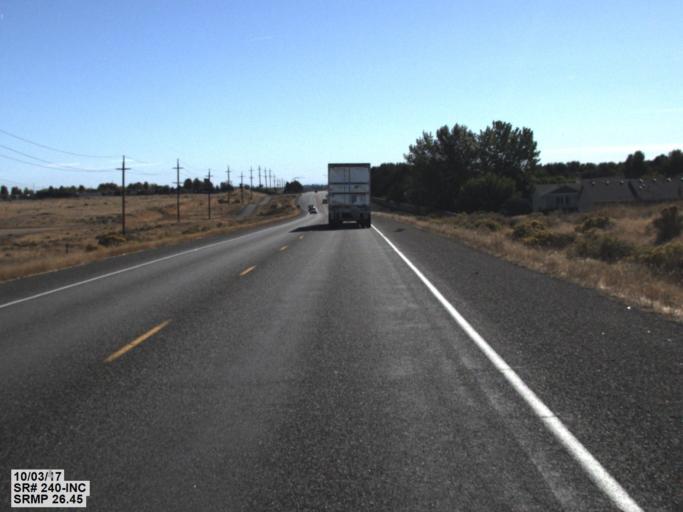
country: US
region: Washington
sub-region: Benton County
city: West Richland
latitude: 46.3297
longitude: -119.3245
